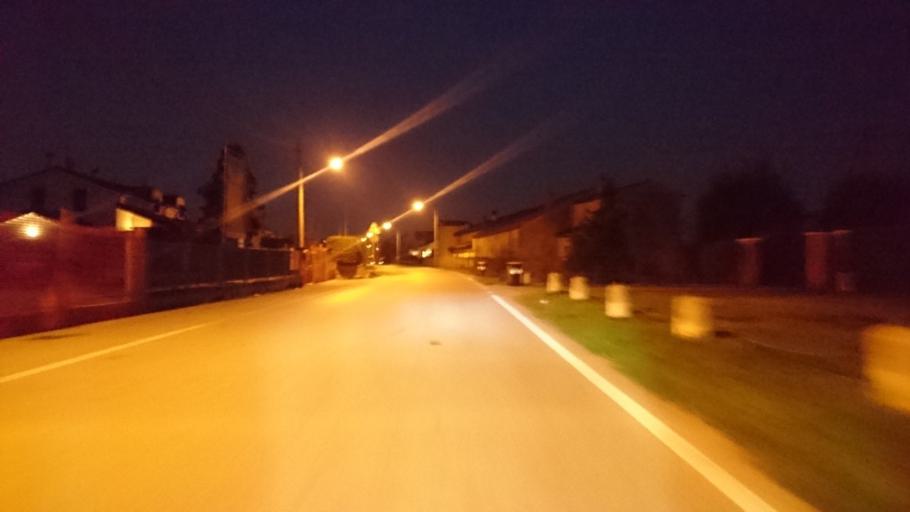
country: IT
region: Veneto
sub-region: Provincia di Padova
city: Mandriola-Sant'Agostino
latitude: 45.3664
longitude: 11.8320
